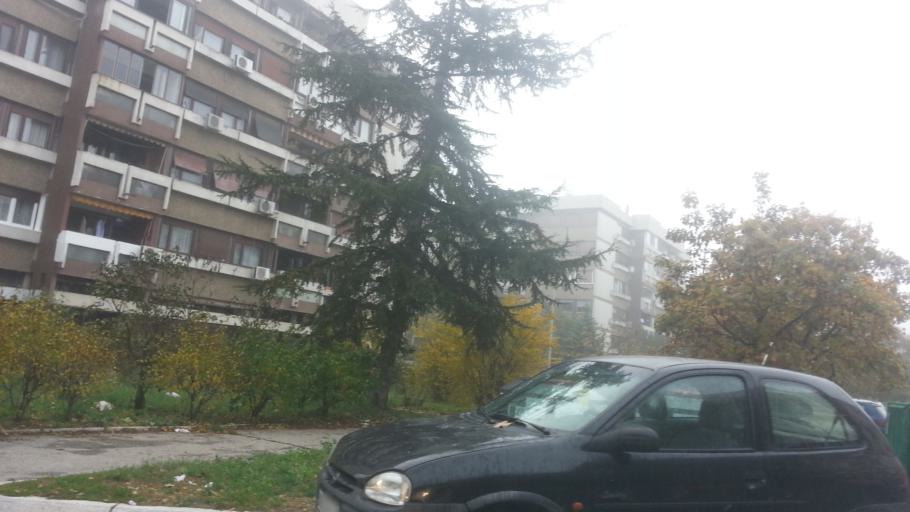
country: RS
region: Central Serbia
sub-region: Belgrade
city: Zemun
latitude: 44.8275
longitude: 20.4161
